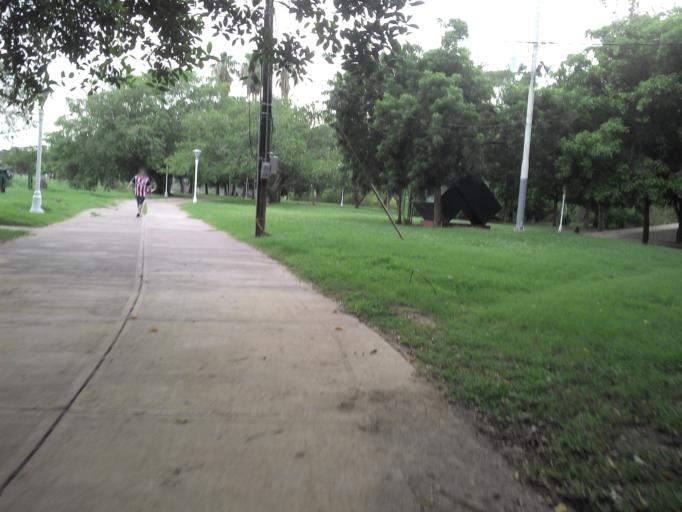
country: MX
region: Sinaloa
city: Culiacan
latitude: 24.8111
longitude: -107.4047
